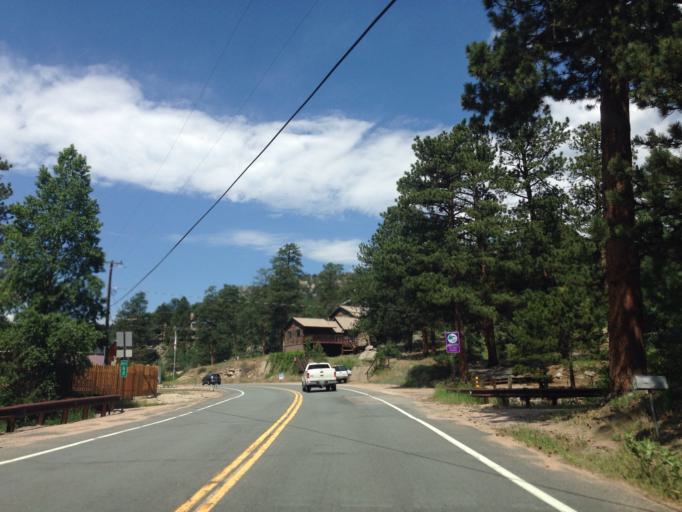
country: US
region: Colorado
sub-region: Larimer County
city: Estes Park
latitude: 40.3939
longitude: -105.4383
